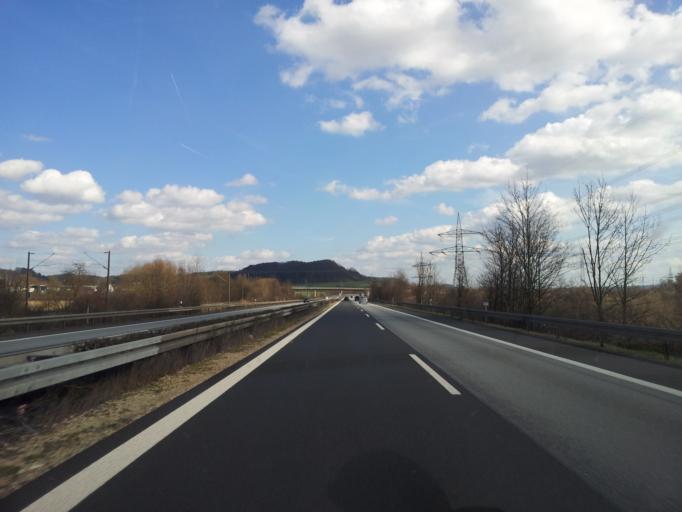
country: DE
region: Bavaria
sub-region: Regierungsbezirk Unterfranken
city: Stettfeld
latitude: 49.9677
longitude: 10.7159
